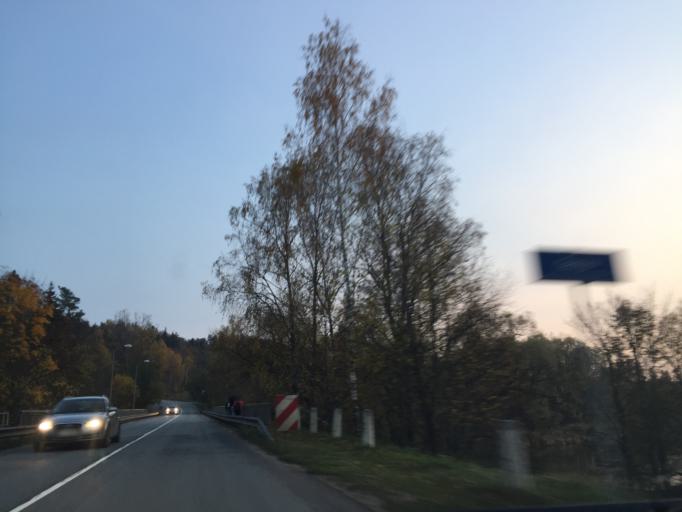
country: LV
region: Cesu Rajons
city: Cesis
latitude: 57.3137
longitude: 25.2267
